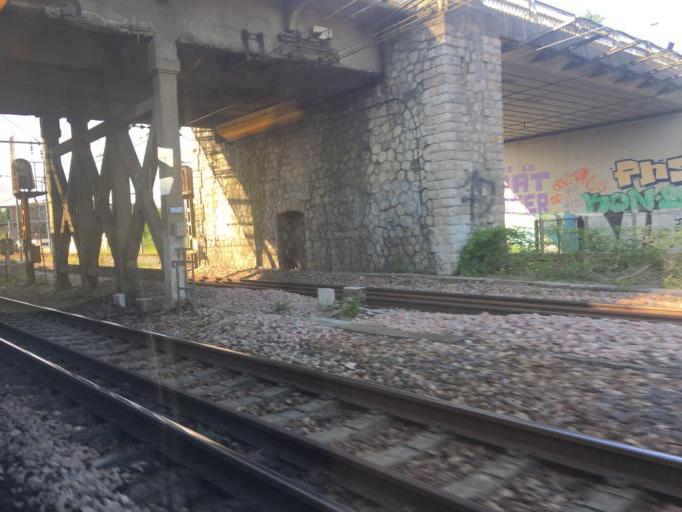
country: FR
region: Ile-de-France
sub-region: Departement de Seine-et-Marne
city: Lieusaint
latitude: 48.6269
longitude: 2.5701
